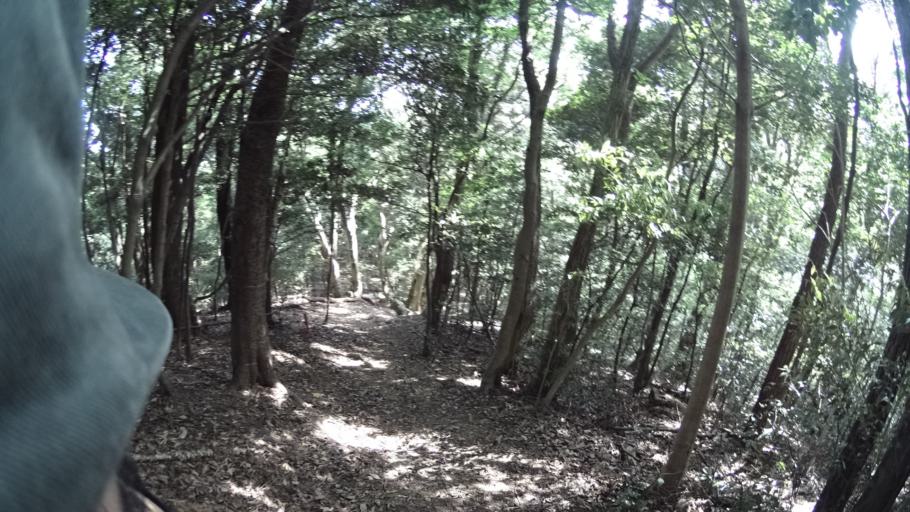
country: JP
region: Shizuoka
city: Kosai-shi
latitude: 34.7800
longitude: 137.4958
